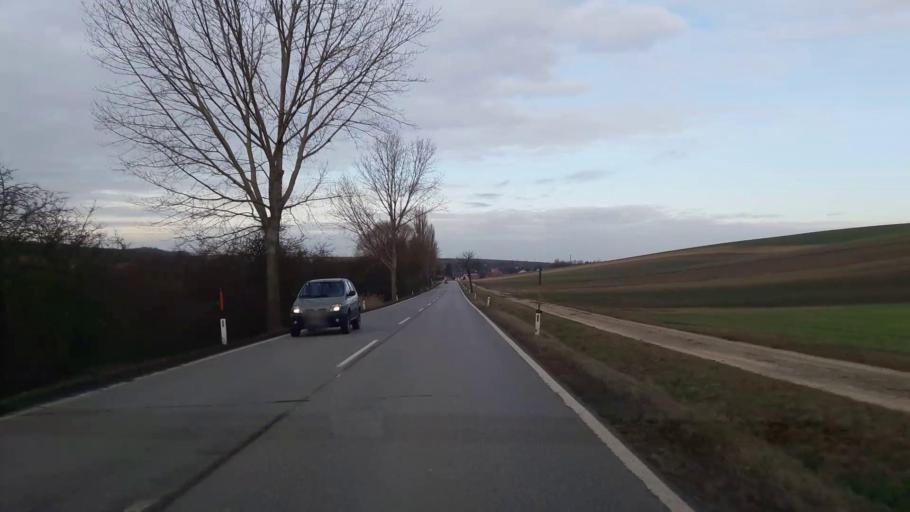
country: AT
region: Lower Austria
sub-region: Politischer Bezirk Mistelbach
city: Staatz
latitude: 48.6535
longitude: 16.5026
